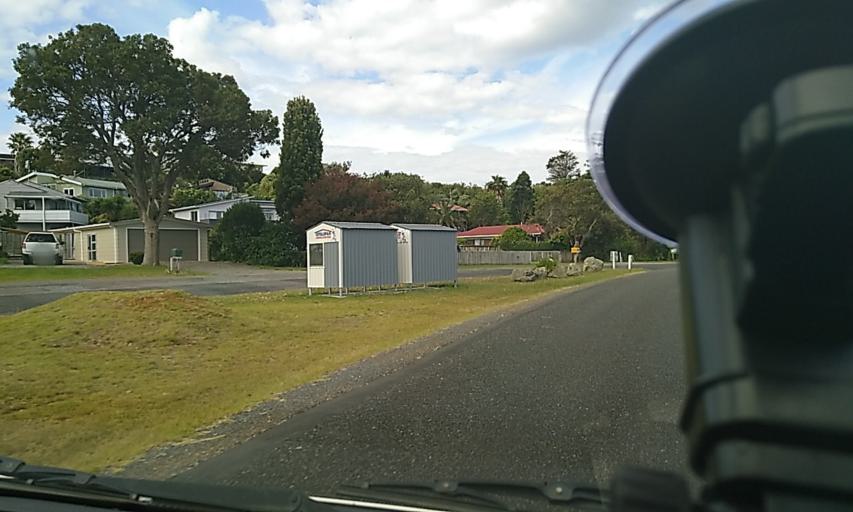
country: NZ
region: Bay of Plenty
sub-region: Western Bay of Plenty District
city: Waihi Beach
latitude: -37.4464
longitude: 175.9576
